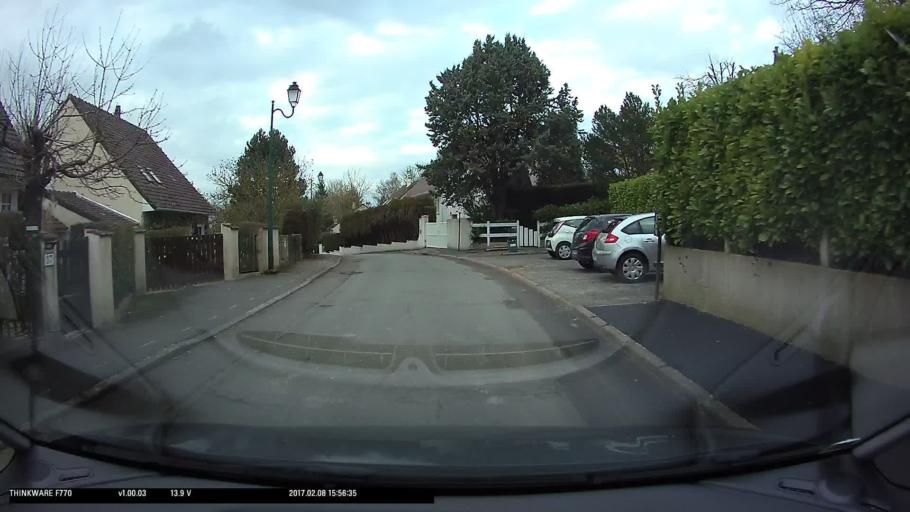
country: FR
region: Ile-de-France
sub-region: Departement du Val-d'Oise
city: Vigny
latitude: 49.0792
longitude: 1.9326
